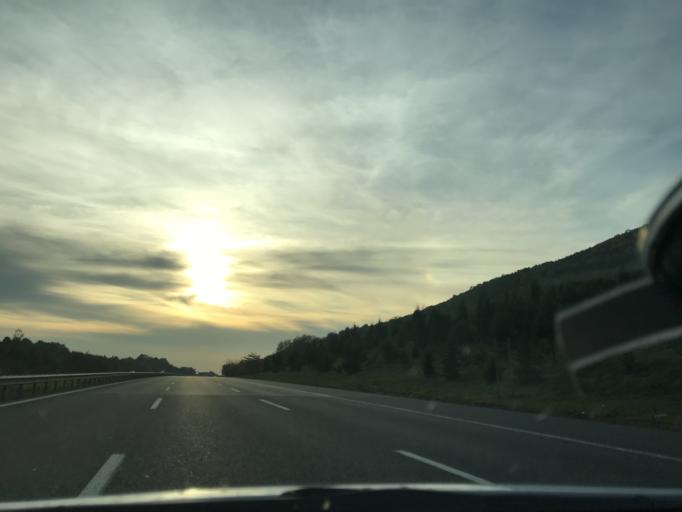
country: TR
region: Duzce
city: Gumusova
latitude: 40.8139
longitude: 30.9056
